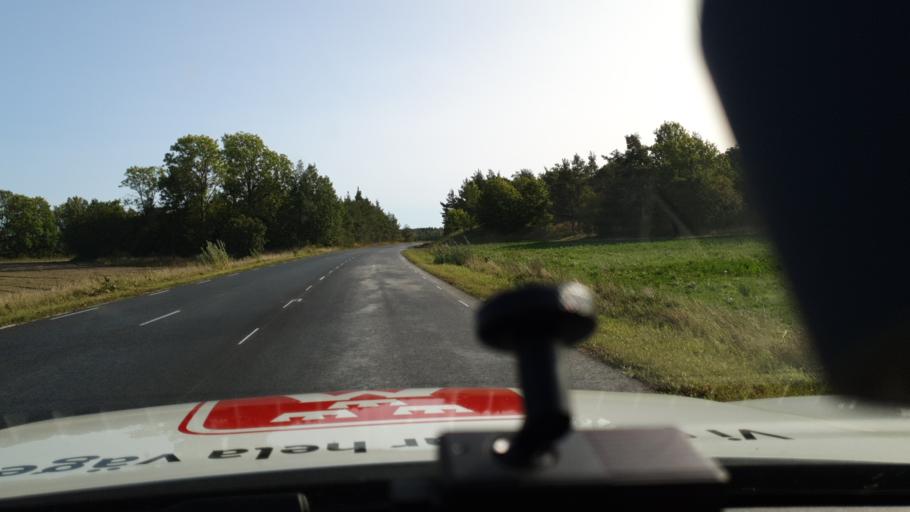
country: SE
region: Gotland
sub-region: Gotland
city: Slite
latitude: 57.7707
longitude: 18.7850
